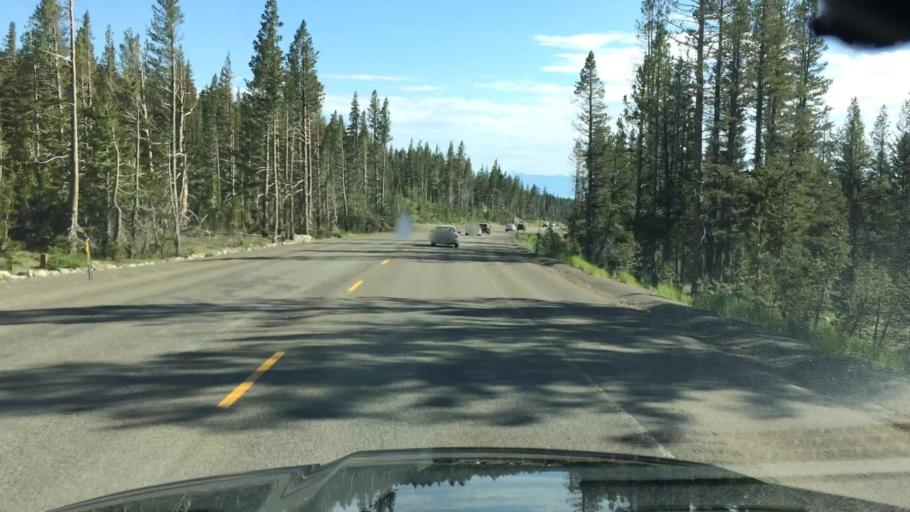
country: US
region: Nevada
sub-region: Washoe County
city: Incline Village
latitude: 39.2967
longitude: -119.9220
